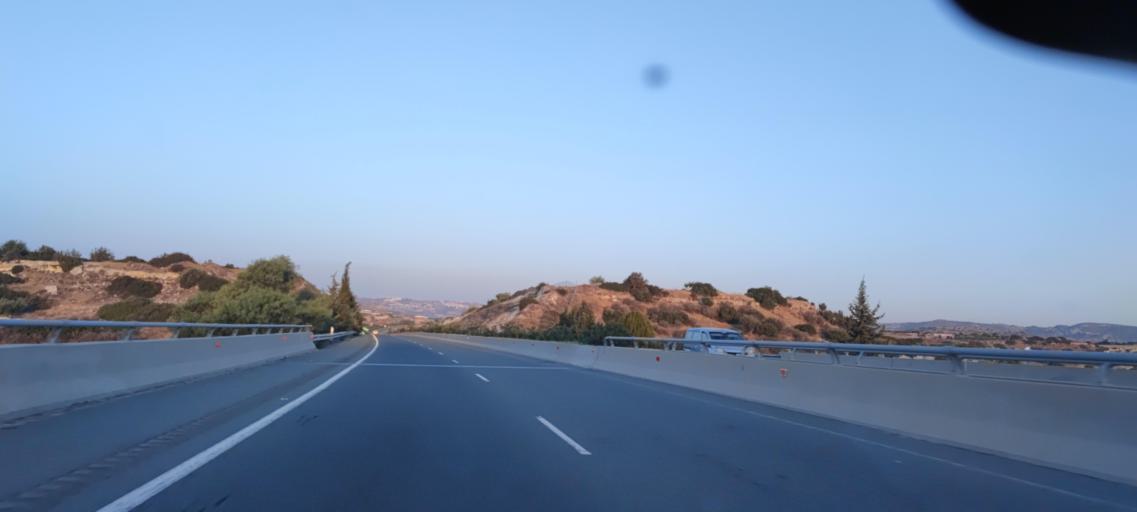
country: CY
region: Limassol
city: Pissouri
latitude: 34.6848
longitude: 32.7817
